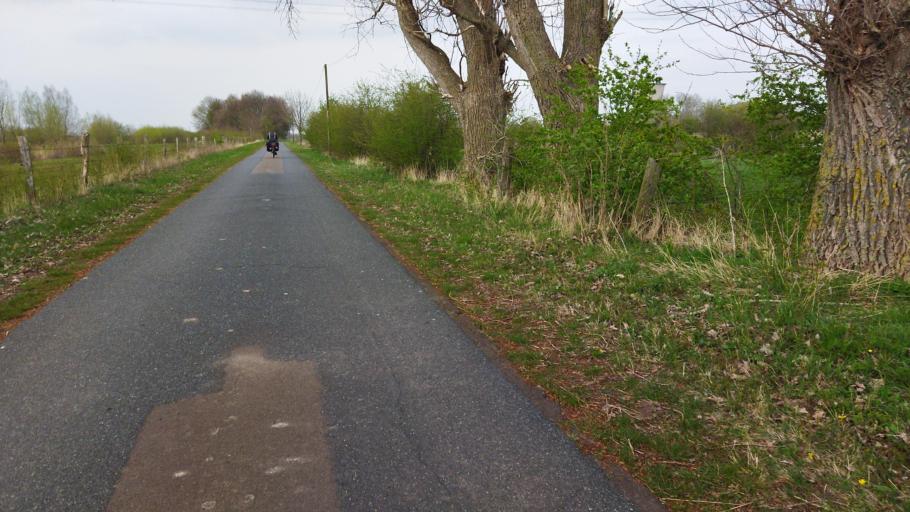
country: DE
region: Lower Saxony
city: Landesbergen
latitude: 52.5438
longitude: 9.1033
